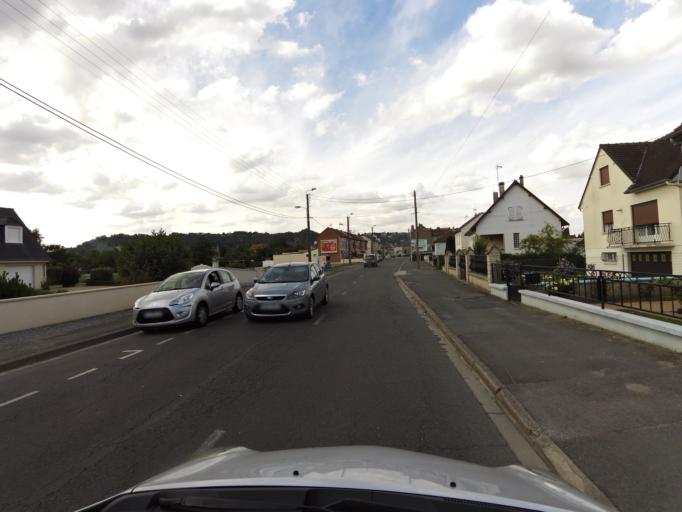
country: FR
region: Picardie
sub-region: Departement de l'Aisne
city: Laon
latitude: 49.5465
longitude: 3.6306
